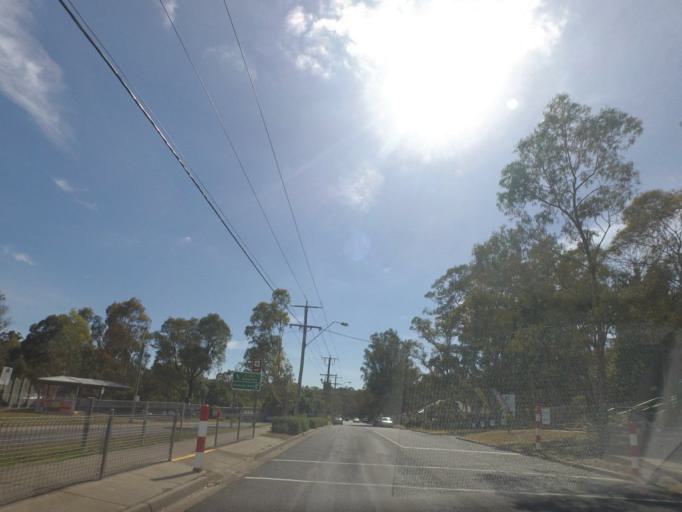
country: AU
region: Victoria
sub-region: Nillumbik
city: Hurstbridge
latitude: -37.6365
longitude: 145.1977
